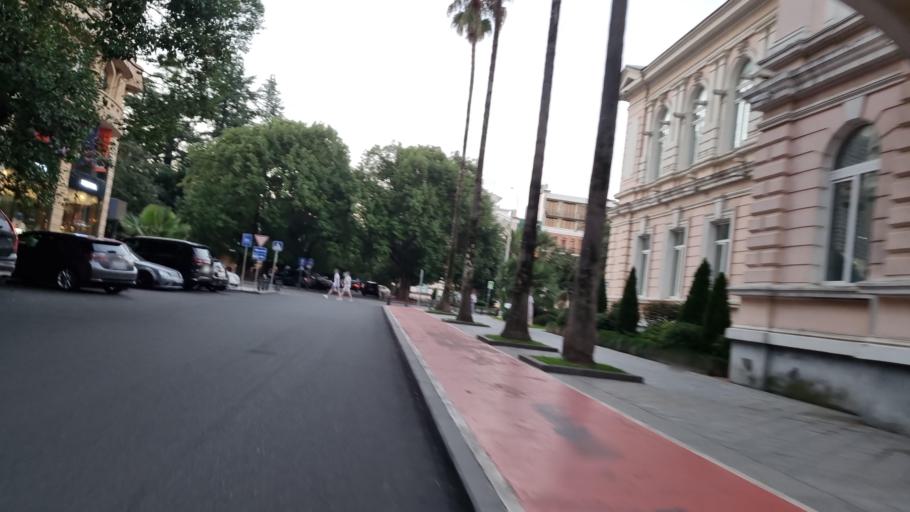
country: GE
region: Ajaria
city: Batumi
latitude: 41.6482
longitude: 41.6352
